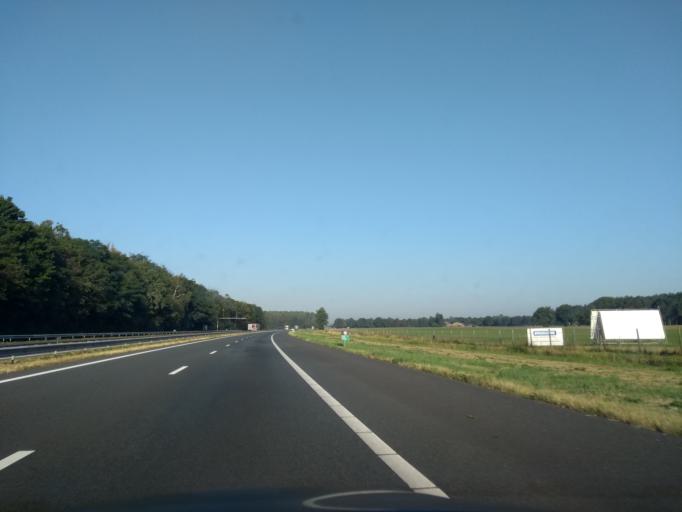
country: NL
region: Gelderland
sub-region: Oude IJsselstreek
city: Wisch
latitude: 51.9441
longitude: 6.4235
